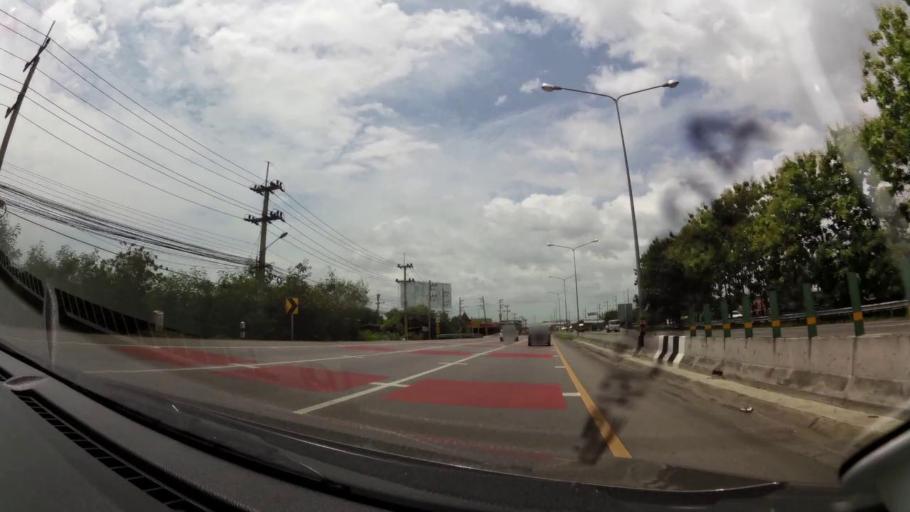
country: TH
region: Phetchaburi
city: Phetchaburi
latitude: 13.1274
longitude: 99.8734
